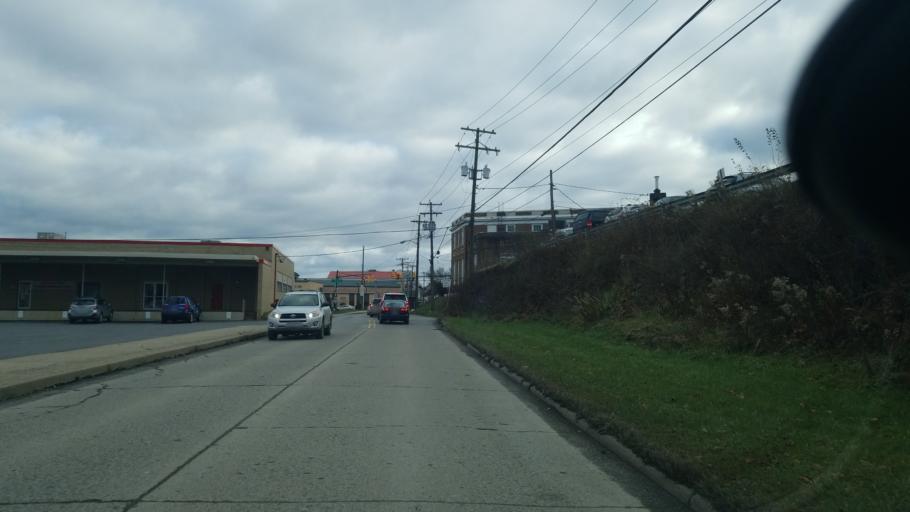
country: US
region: Pennsylvania
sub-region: Clearfield County
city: DuBois
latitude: 41.1202
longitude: -78.7610
